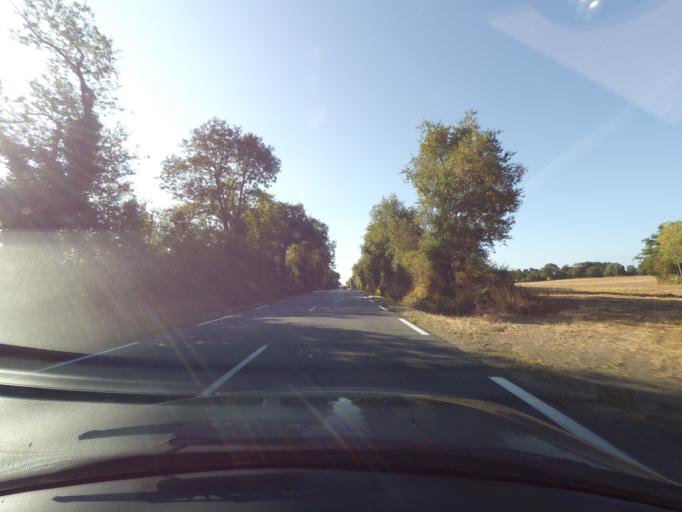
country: FR
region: Poitou-Charentes
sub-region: Departement des Deux-Sevres
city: Viennay
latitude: 46.7046
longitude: -0.2838
